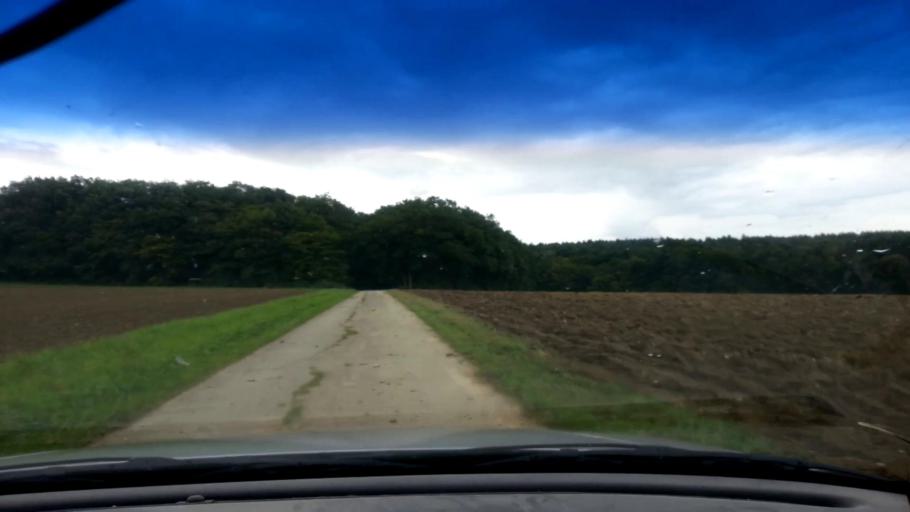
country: DE
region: Bavaria
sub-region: Upper Franconia
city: Litzendorf
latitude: 49.9372
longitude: 11.0009
